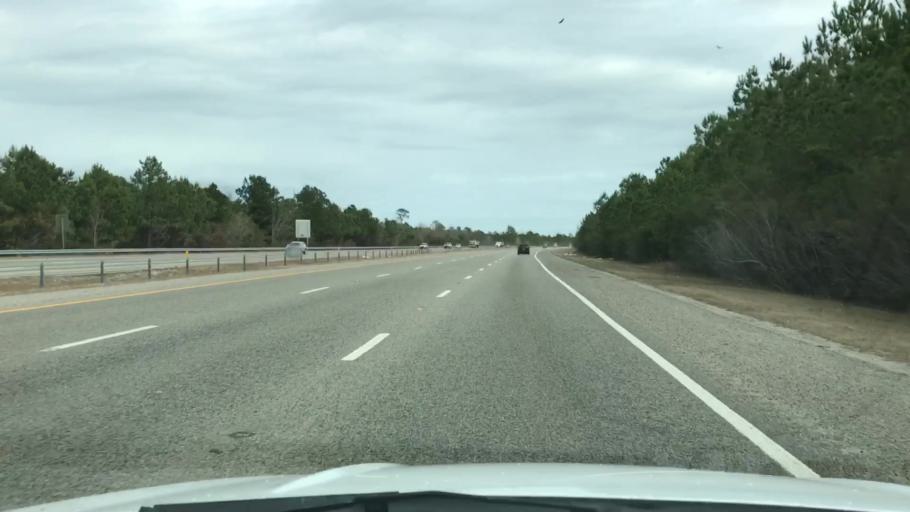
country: US
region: South Carolina
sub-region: Horry County
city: Forestbrook
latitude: 33.7218
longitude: -78.9952
